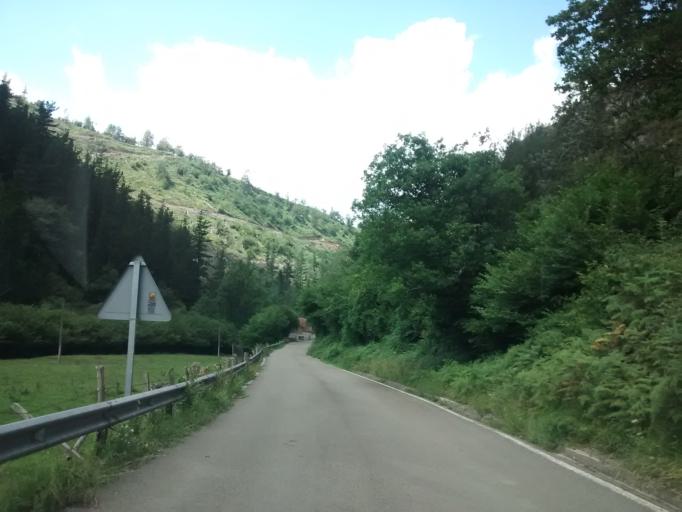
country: ES
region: Cantabria
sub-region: Provincia de Cantabria
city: Ruente
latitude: 43.1937
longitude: -4.2855
